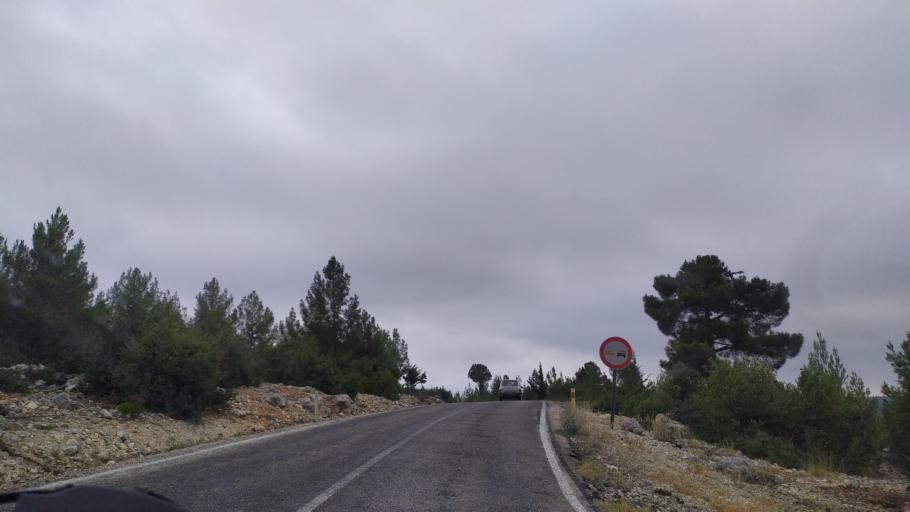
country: TR
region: Mersin
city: Silifke
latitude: 36.5444
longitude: 33.9267
